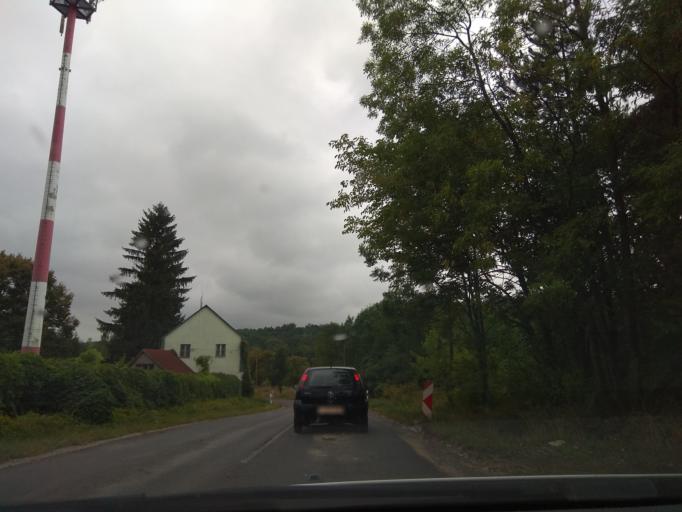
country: HU
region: Borsod-Abauj-Zemplen
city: Harsany
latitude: 47.9997
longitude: 20.7586
